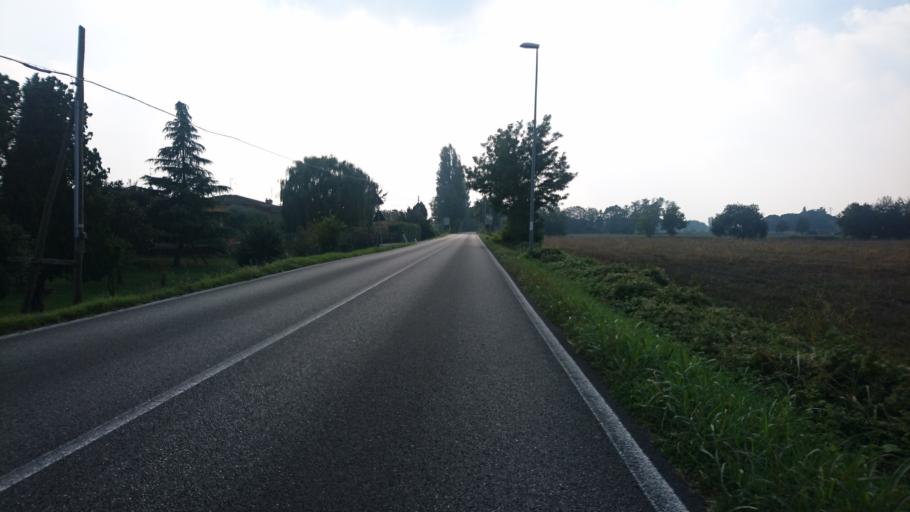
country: IT
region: Veneto
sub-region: Provincia di Rovigo
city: Grignano Polesine
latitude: 45.0462
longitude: 11.7761
